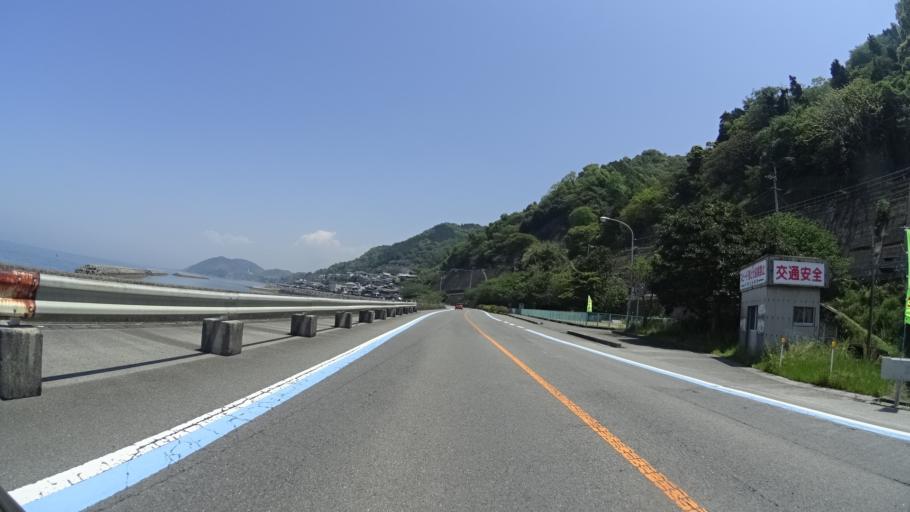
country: JP
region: Ehime
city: Iyo
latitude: 33.6918
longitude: 132.6457
